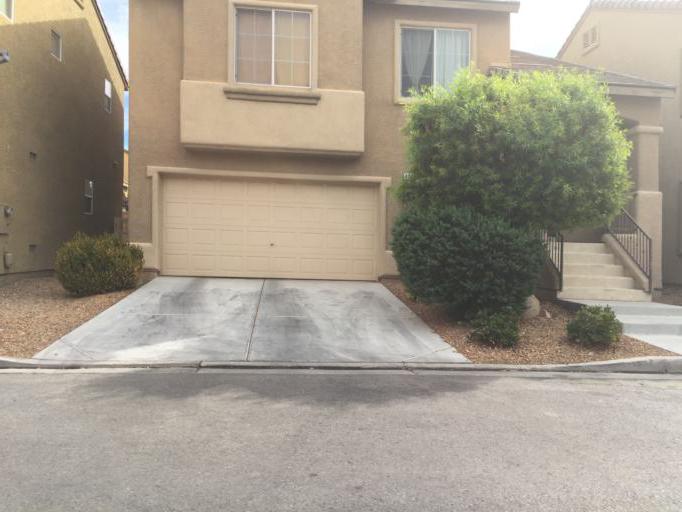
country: US
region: Nevada
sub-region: Clark County
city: Whitney
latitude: 36.1159
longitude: -115.0345
